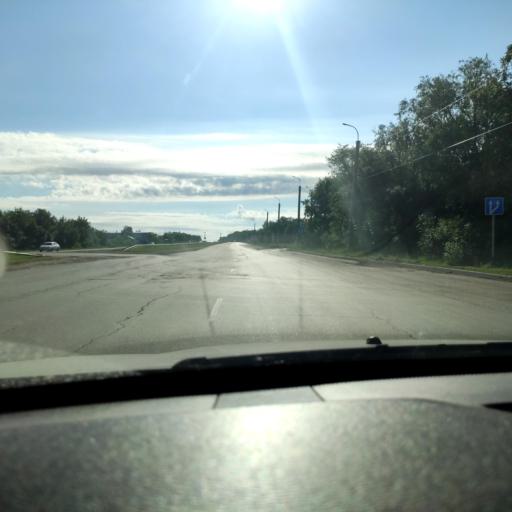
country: RU
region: Samara
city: Smyshlyayevka
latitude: 53.2583
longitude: 50.4420
